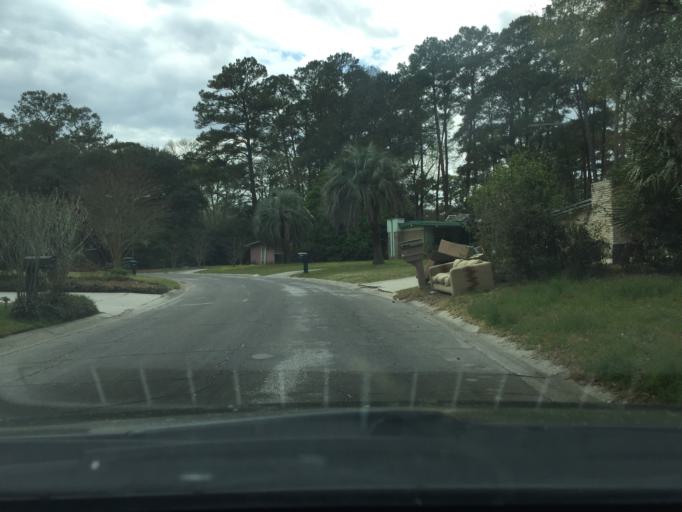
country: US
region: Georgia
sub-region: Chatham County
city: Montgomery
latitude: 31.9824
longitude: -81.1069
